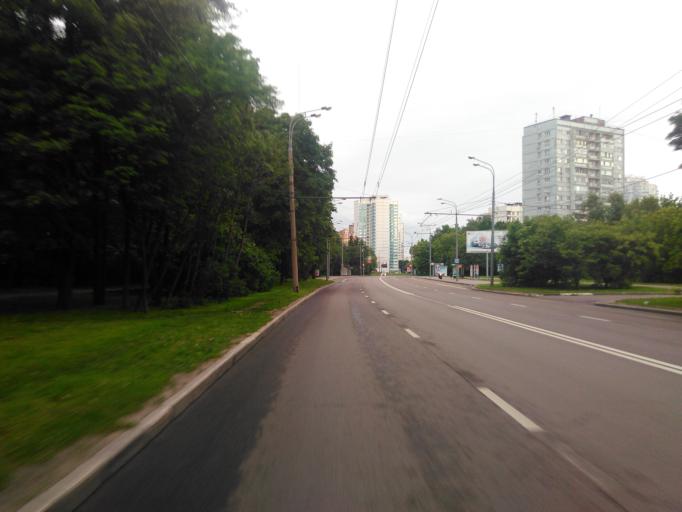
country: RU
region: Moscow
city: Troparevo
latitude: 55.6572
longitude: 37.4918
